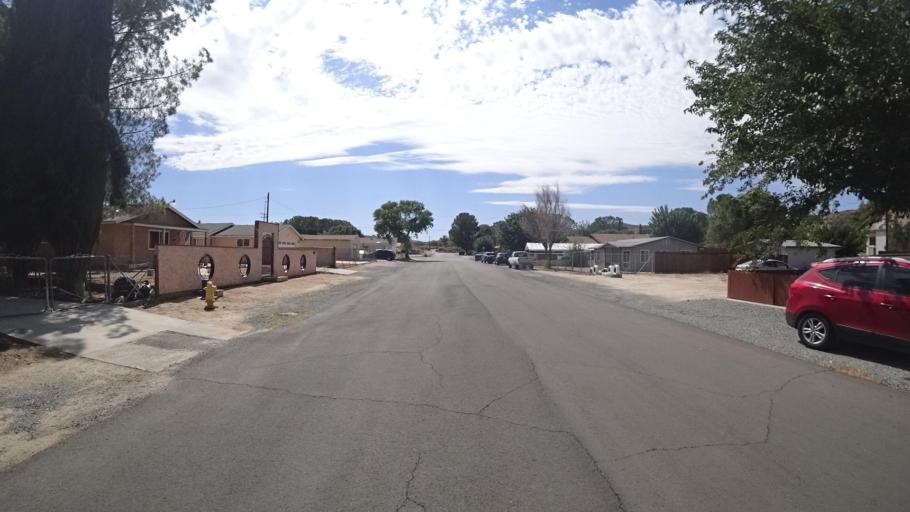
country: MX
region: Baja California
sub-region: Tecate
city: Cereso del Hongo
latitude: 32.6189
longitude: -116.1896
